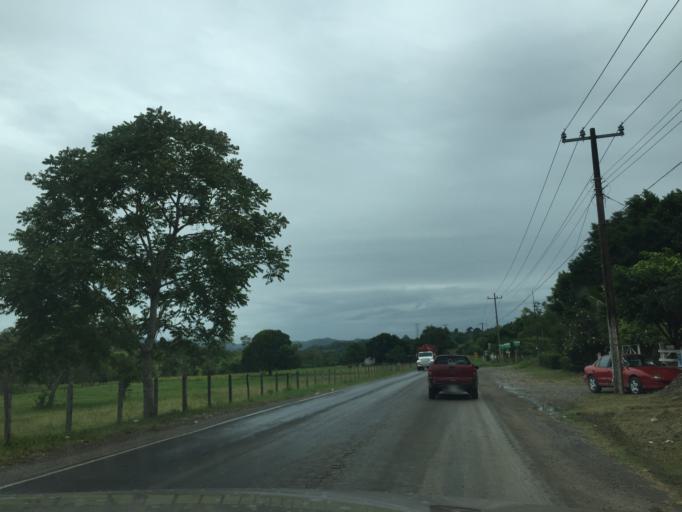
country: MX
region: Veracruz
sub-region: Papantla
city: El Chote
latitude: 20.4420
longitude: -97.4051
